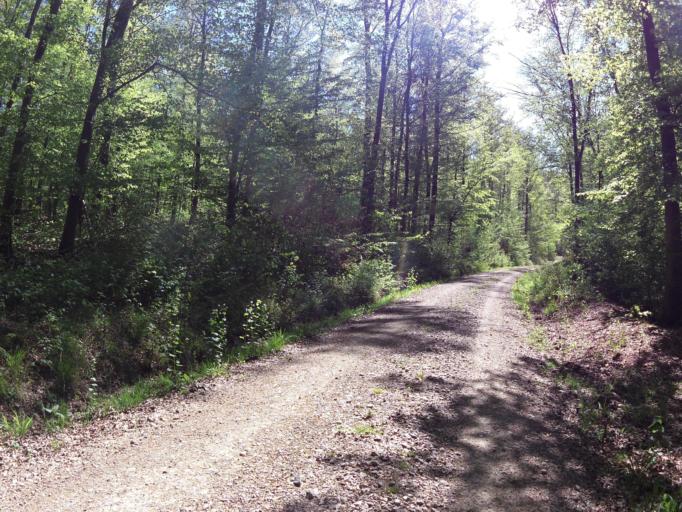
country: DE
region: Thuringia
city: Wolfsburg-Unkeroda
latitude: 50.9678
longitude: 10.2687
